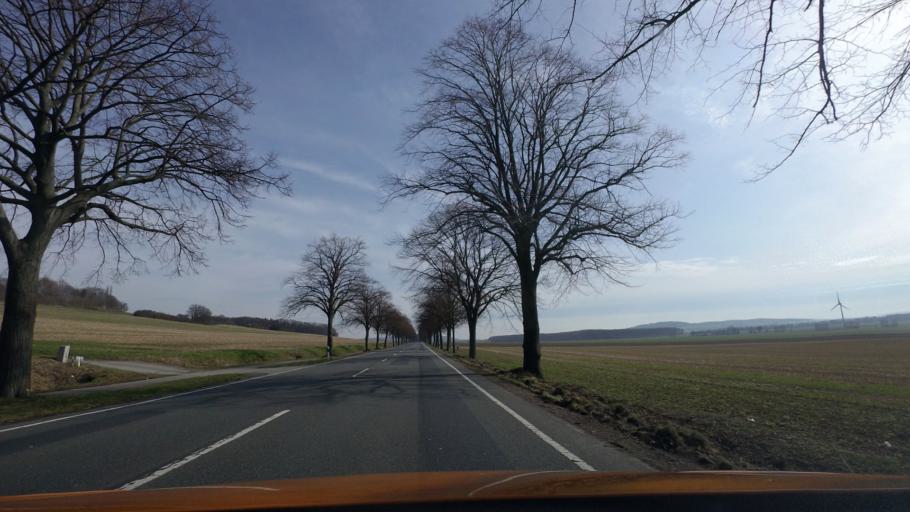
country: DE
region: Lower Saxony
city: Grossgoltern
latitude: 52.3405
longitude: 9.5285
